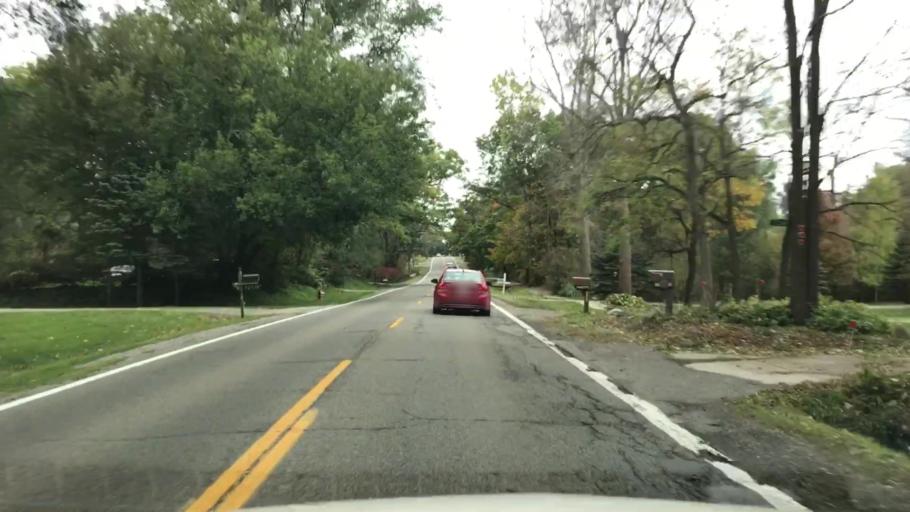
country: US
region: Michigan
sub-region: Macomb County
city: Shelby
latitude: 42.6805
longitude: -83.0670
